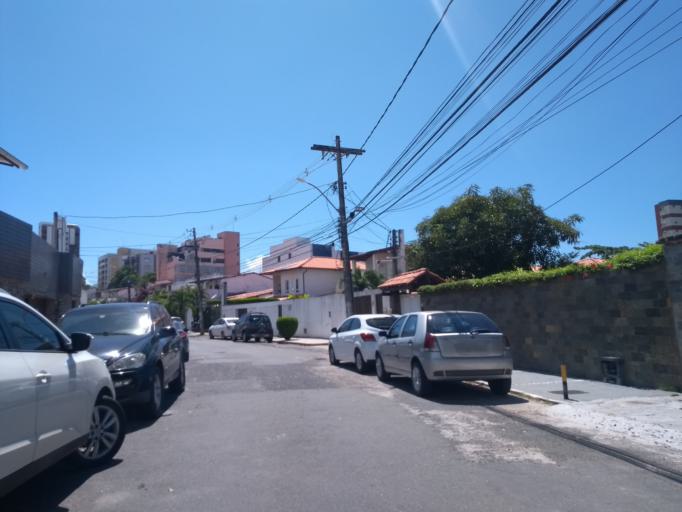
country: BR
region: Bahia
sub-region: Salvador
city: Salvador
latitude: -12.9935
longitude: -38.4598
